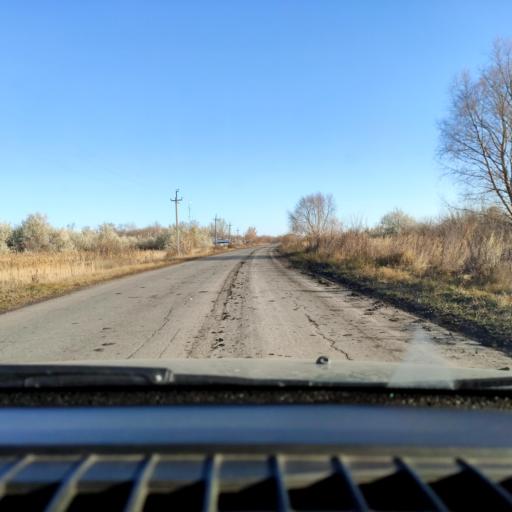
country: RU
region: Samara
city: Tol'yatti
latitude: 53.6371
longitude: 49.3100
